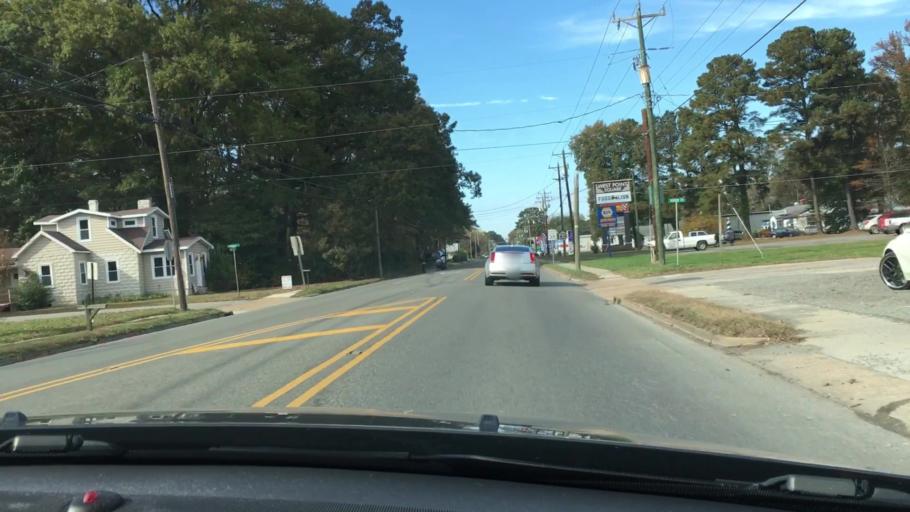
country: US
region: Virginia
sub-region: King William County
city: West Point
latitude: 37.5497
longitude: -76.8082
